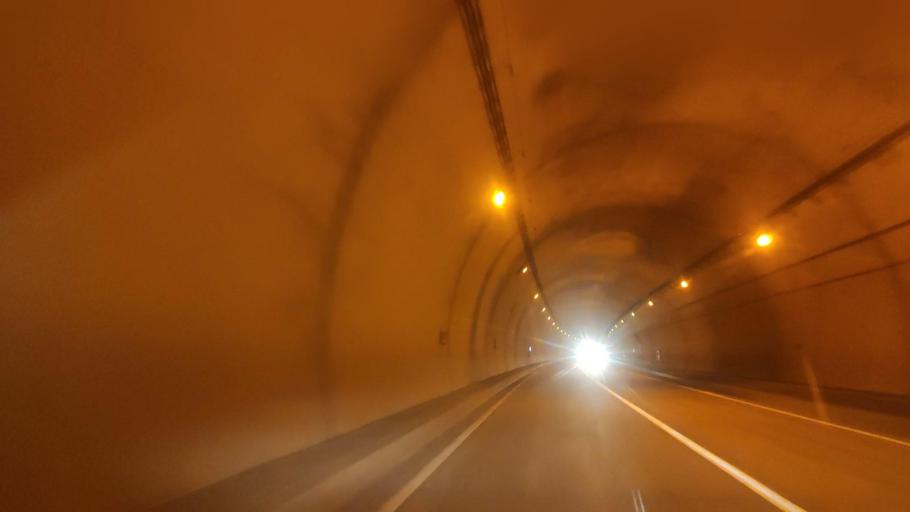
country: JP
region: Hokkaido
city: Date
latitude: 42.5614
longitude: 140.7812
